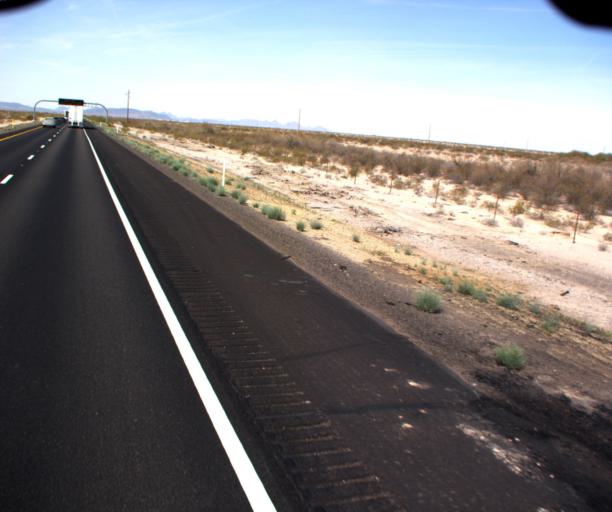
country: US
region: Arizona
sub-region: La Paz County
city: Salome
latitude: 33.6206
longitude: -113.6956
